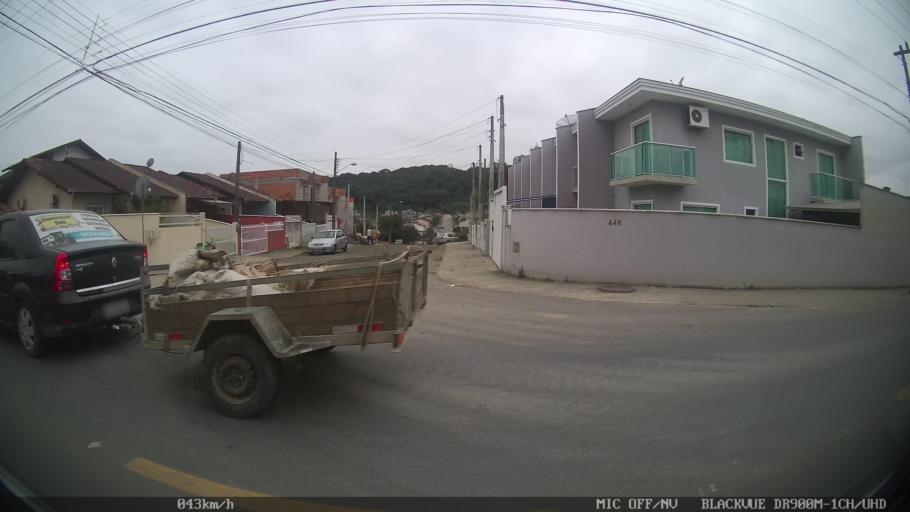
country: BR
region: Santa Catarina
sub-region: Joinville
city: Joinville
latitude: -26.3671
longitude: -48.8242
